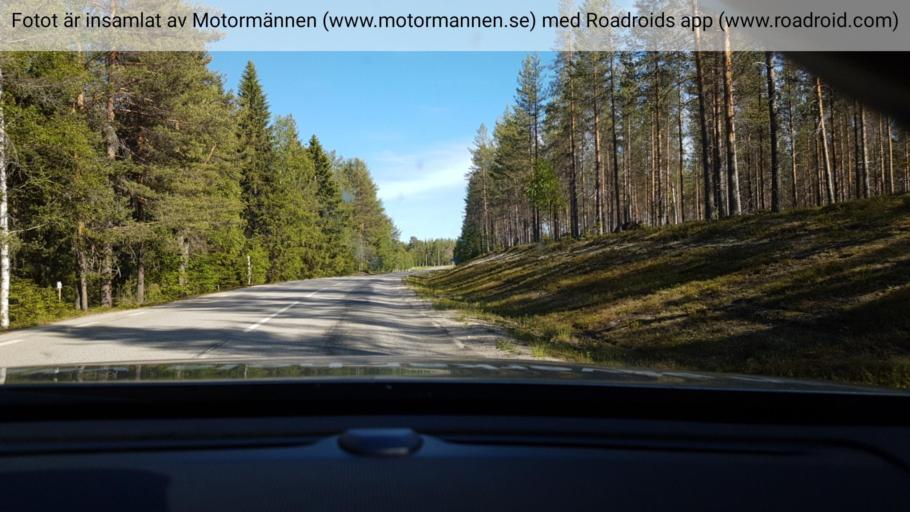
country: SE
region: Vaesterbotten
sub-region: Norsjo Kommun
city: Norsjoe
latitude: 64.7386
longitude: 19.1213
